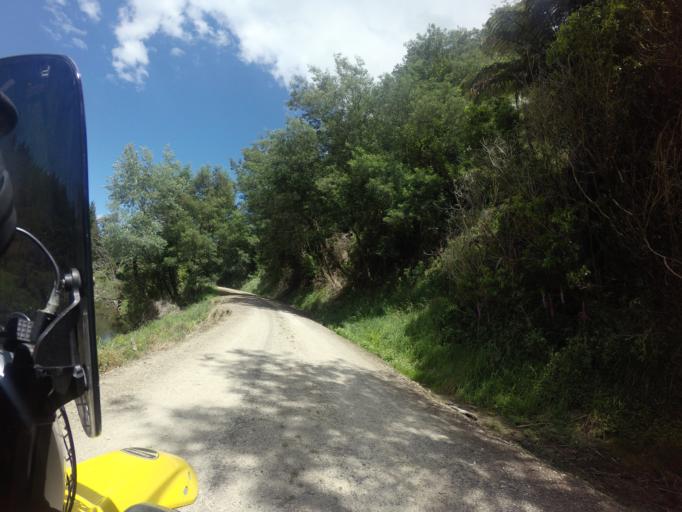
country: NZ
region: Hawke's Bay
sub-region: Wairoa District
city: Wairoa
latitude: -38.9694
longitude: 177.6692
